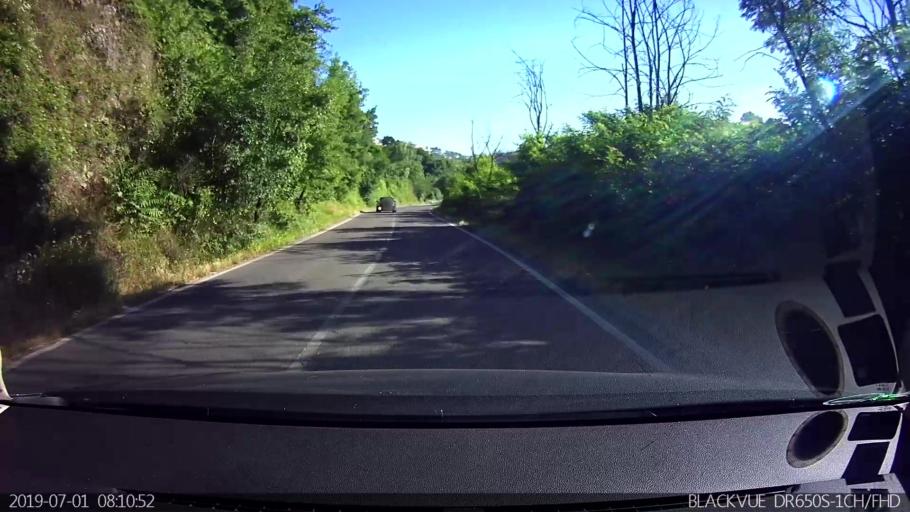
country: IT
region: Latium
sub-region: Provincia di Frosinone
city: Sant'Angelo in Villa-Giglio
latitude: 41.6731
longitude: 13.4216
